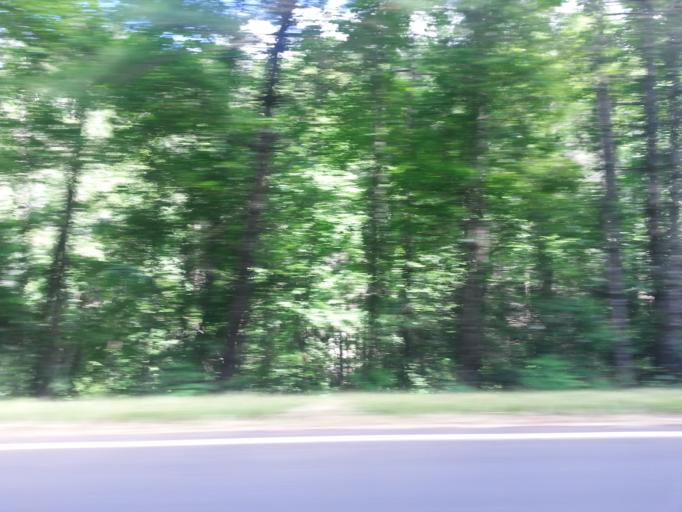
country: US
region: Georgia
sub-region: Towns County
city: Hiawassee
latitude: 34.8322
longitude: -83.7482
